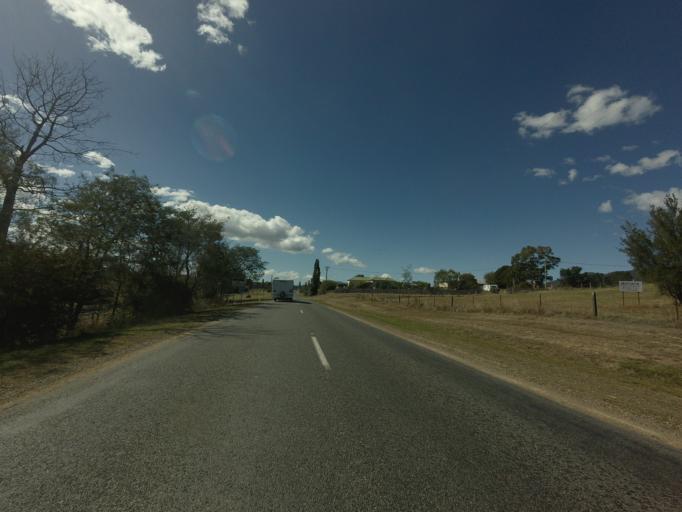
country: AU
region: Tasmania
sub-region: Break O'Day
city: St Helens
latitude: -41.6431
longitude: 147.9623
